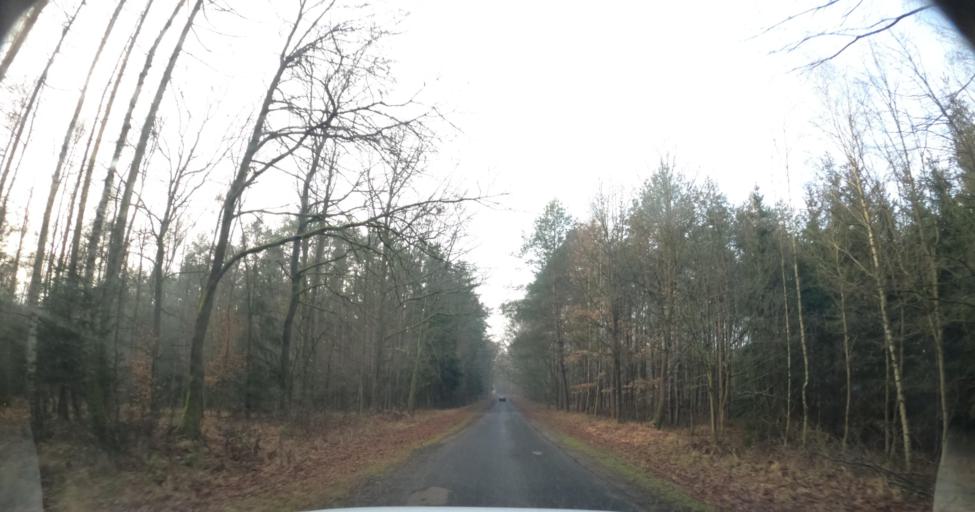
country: PL
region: West Pomeranian Voivodeship
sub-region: Powiat mysliborski
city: Boleszkowice
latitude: 52.7125
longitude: 14.5556
